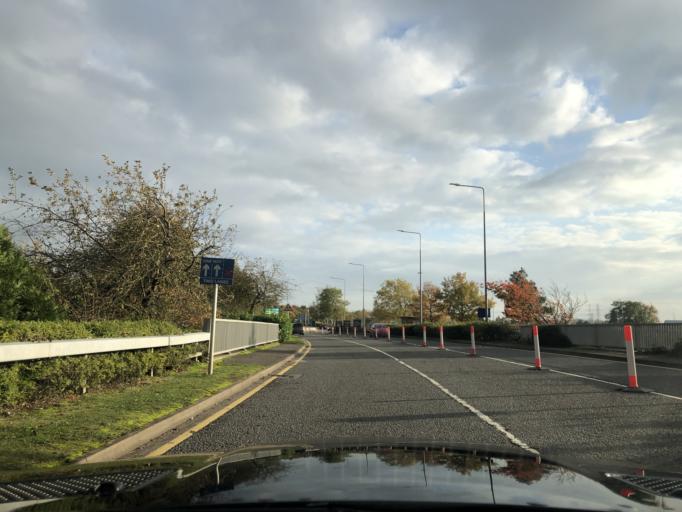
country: GB
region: England
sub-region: Solihull
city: Bickenhill
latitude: 52.4589
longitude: -1.7138
